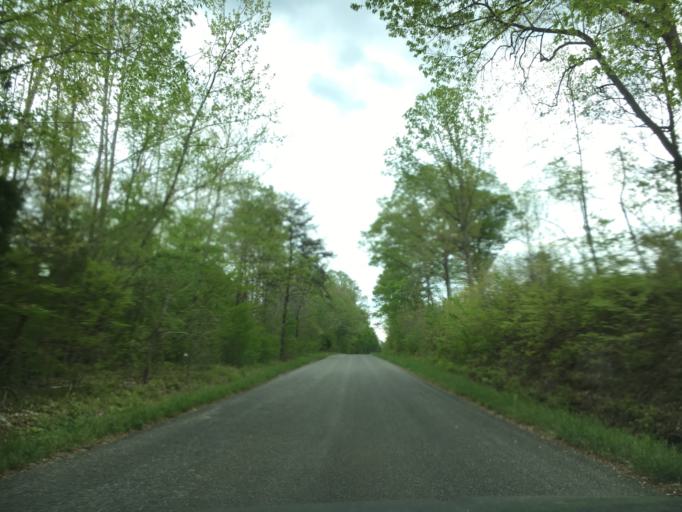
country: US
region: Virginia
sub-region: Halifax County
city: Halifax
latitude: 36.8013
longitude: -78.9267
